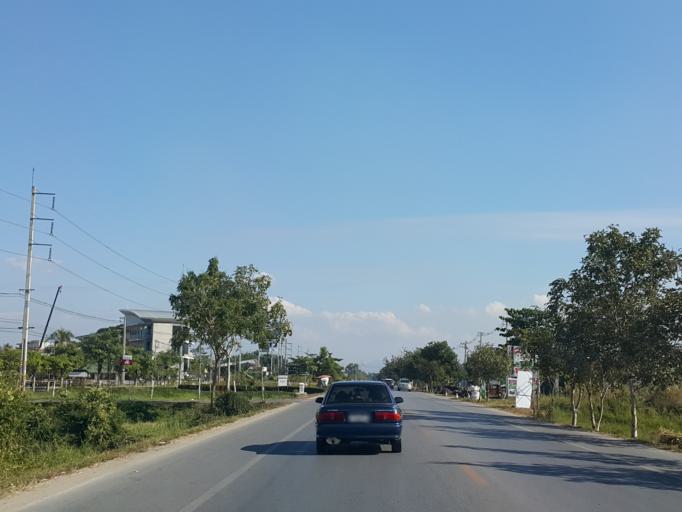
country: TH
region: Chiang Mai
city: San Sai
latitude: 18.8364
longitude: 99.0316
